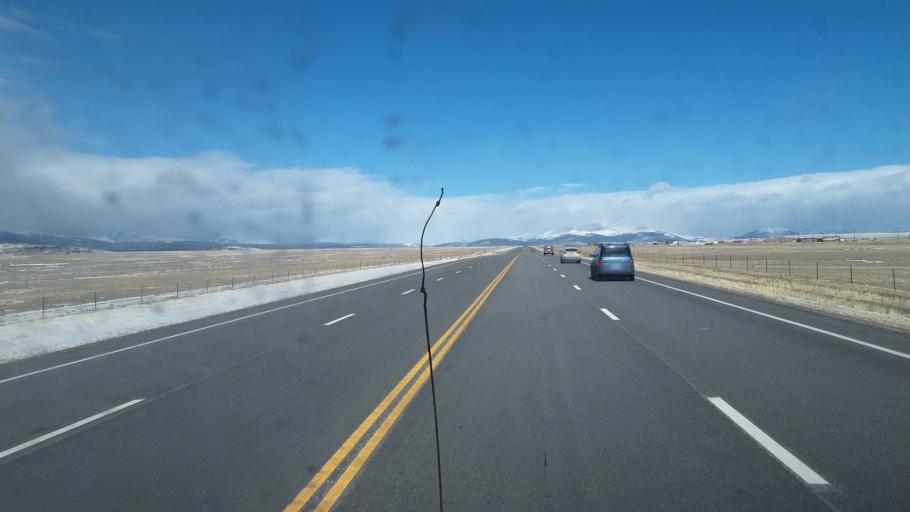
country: US
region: Colorado
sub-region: Park County
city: Fairplay
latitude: 39.1120
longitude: -105.9917
